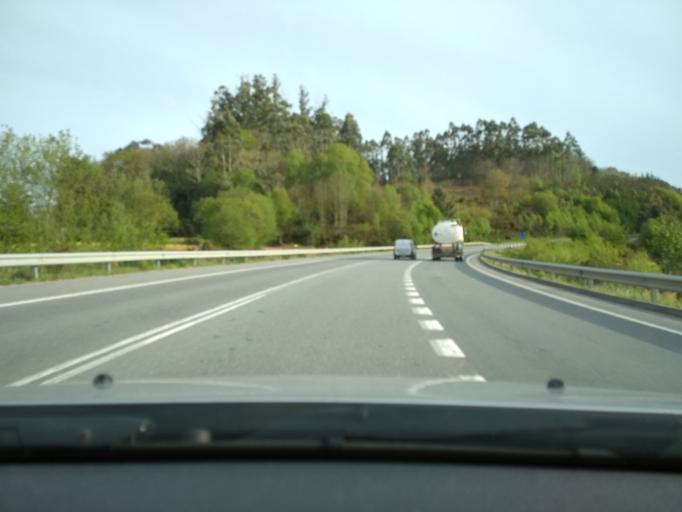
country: ES
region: Galicia
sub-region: Provincia da Coruna
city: Cerceda
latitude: 43.2166
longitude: -8.4556
